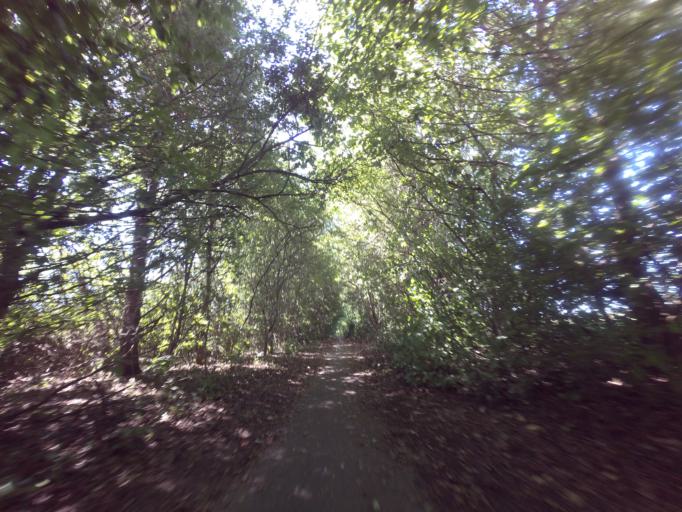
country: GB
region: England
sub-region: Kent
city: Eastry
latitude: 51.2312
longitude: 1.3048
